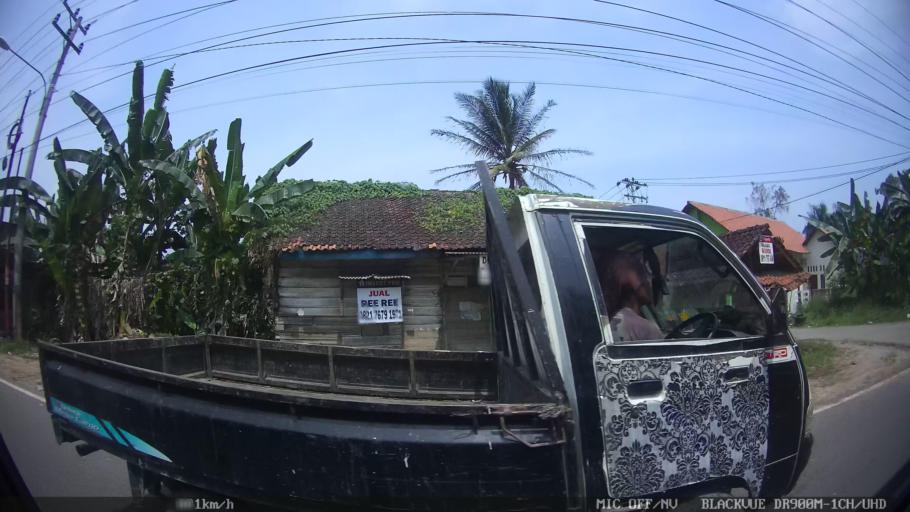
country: ID
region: Lampung
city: Bandarlampung
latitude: -5.4575
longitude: 105.2454
